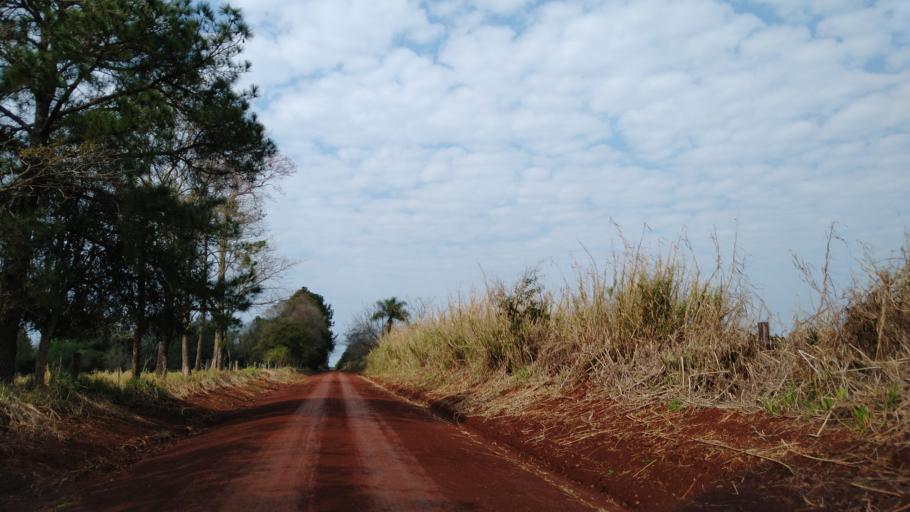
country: AR
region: Misiones
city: Capiovi
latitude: -26.9556
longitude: -55.0625
